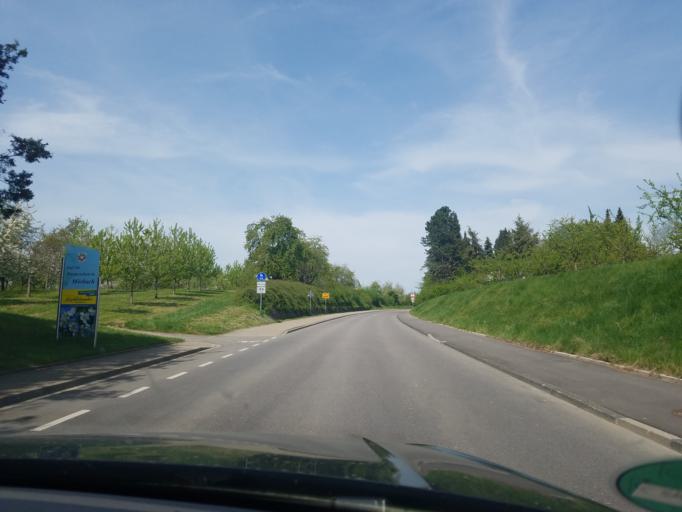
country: DE
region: Baden-Wuerttemberg
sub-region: Freiburg Region
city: Achern
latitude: 48.6001
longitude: 8.0652
